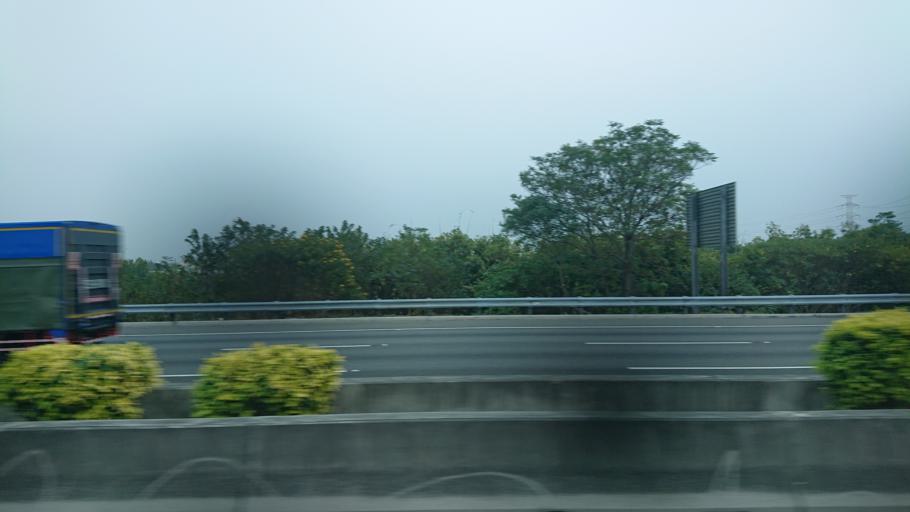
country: TW
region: Taiwan
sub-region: Nantou
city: Nantou
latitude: 23.8983
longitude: 120.4965
